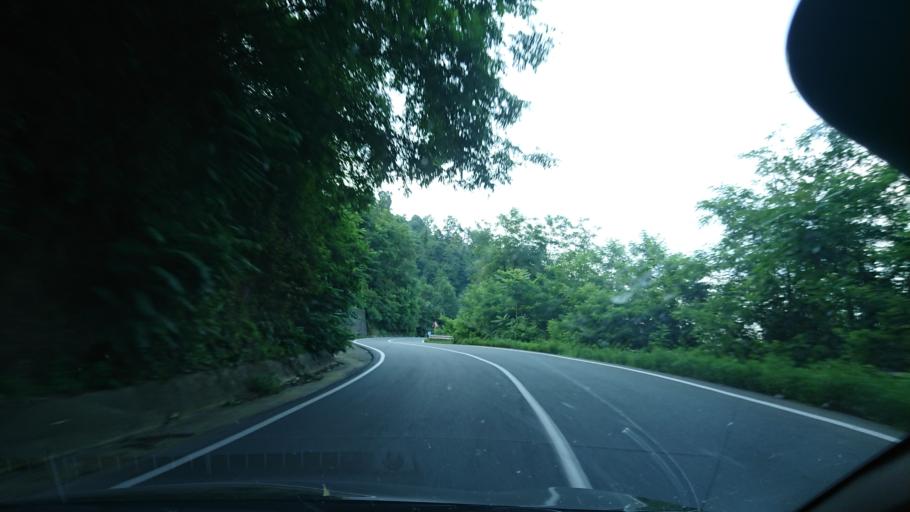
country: TR
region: Rize
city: Cayeli
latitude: 41.0717
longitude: 40.7114
